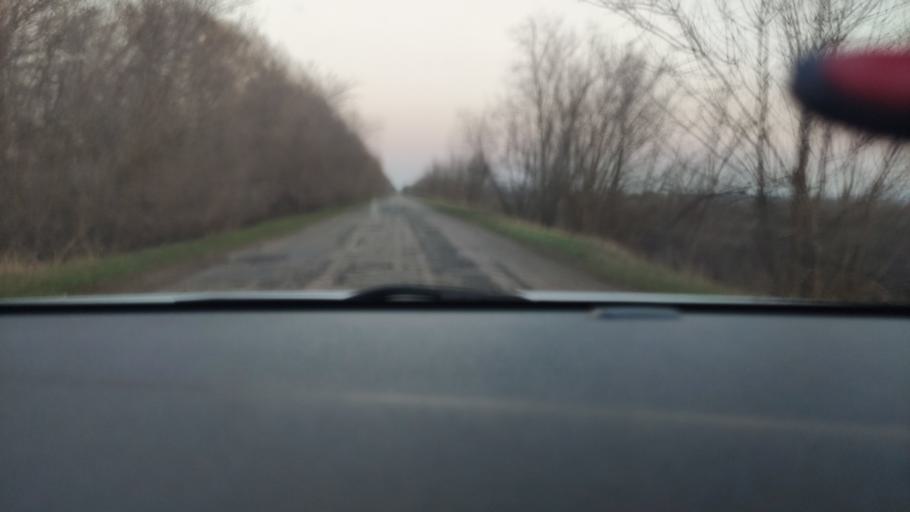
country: RU
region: Voronezj
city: Uryv-Pokrovka
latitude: 51.1366
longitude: 39.0860
